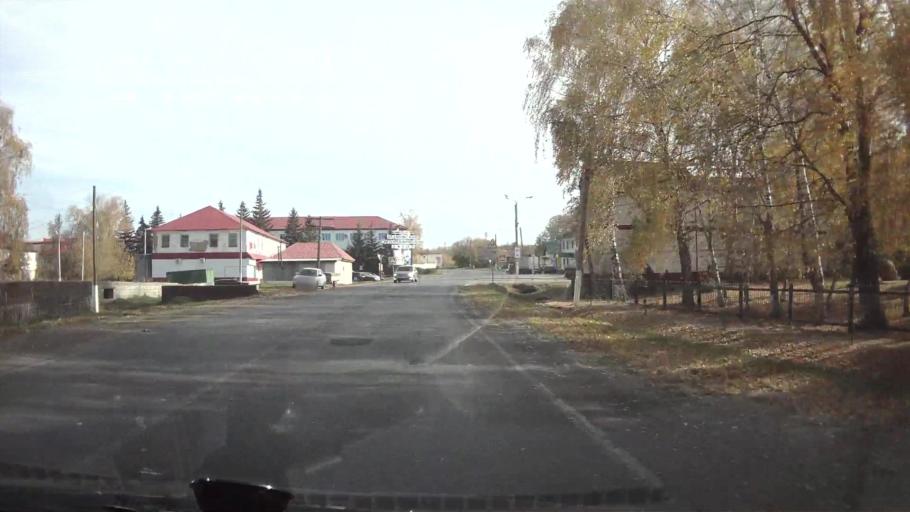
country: RU
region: Mordoviya
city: Turgenevo
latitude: 54.8463
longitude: 46.3363
